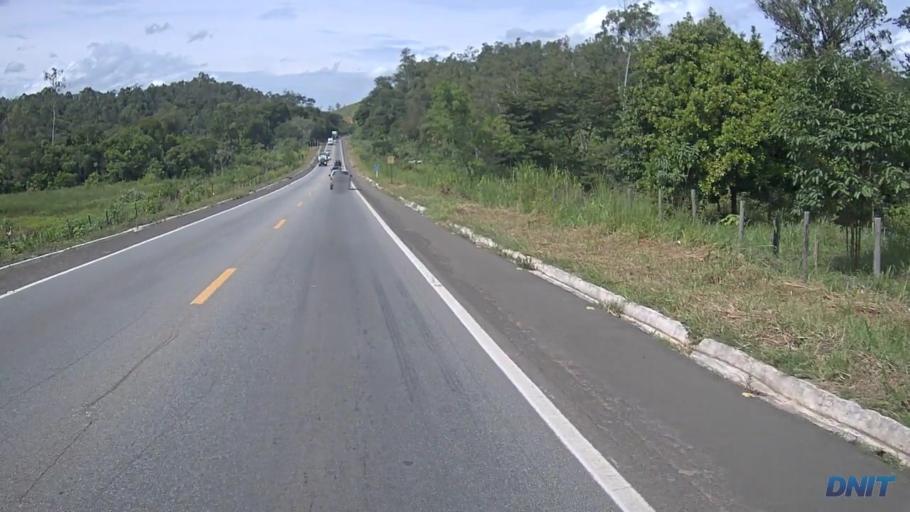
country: BR
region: Minas Gerais
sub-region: Ipatinga
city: Ipatinga
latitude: -19.4300
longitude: -42.5040
